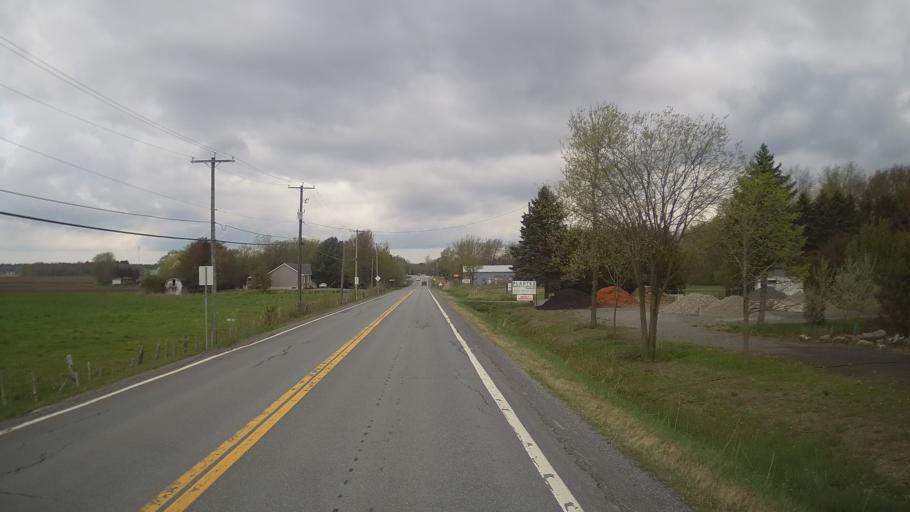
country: CA
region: Quebec
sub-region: Monteregie
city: Farnham
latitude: 45.2676
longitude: -72.9427
